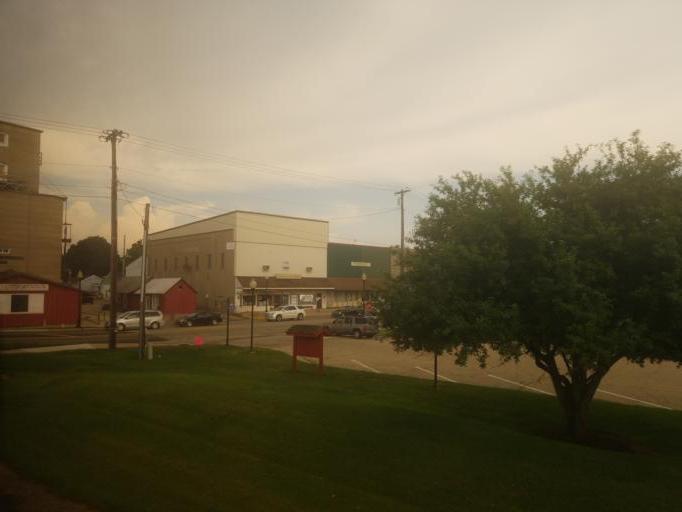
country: US
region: Illinois
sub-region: Bureau County
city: Princeton
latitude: 41.3854
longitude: -89.4657
